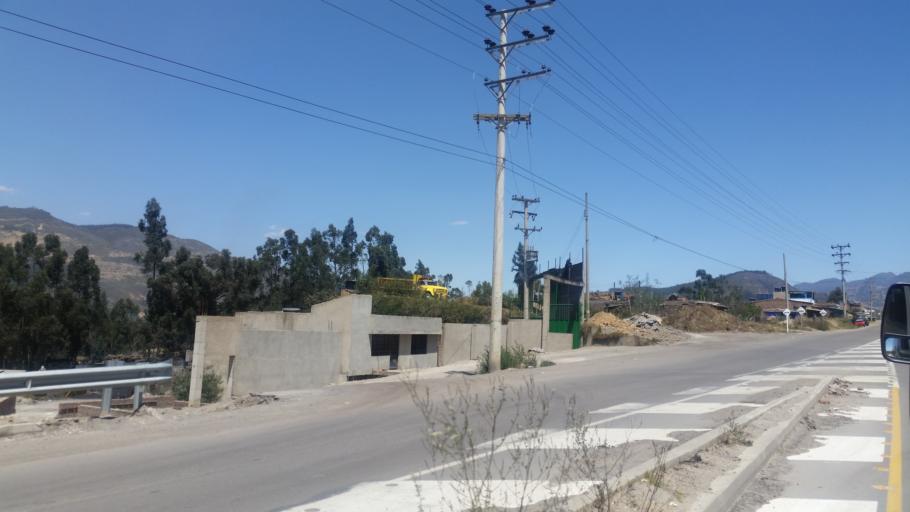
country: CO
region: Boyaca
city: Mongui
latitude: 5.7601
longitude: -72.8867
